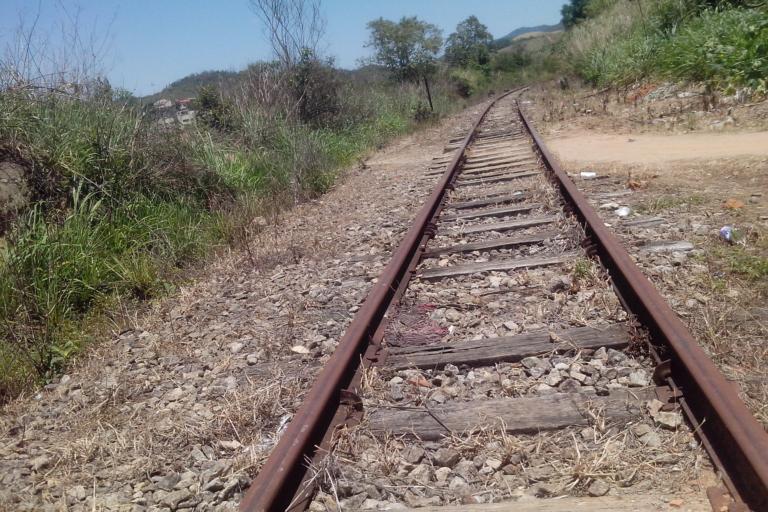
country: BR
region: Rio de Janeiro
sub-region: Rio Bonito
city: Rio Bonito
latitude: -22.7088
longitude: -42.6434
